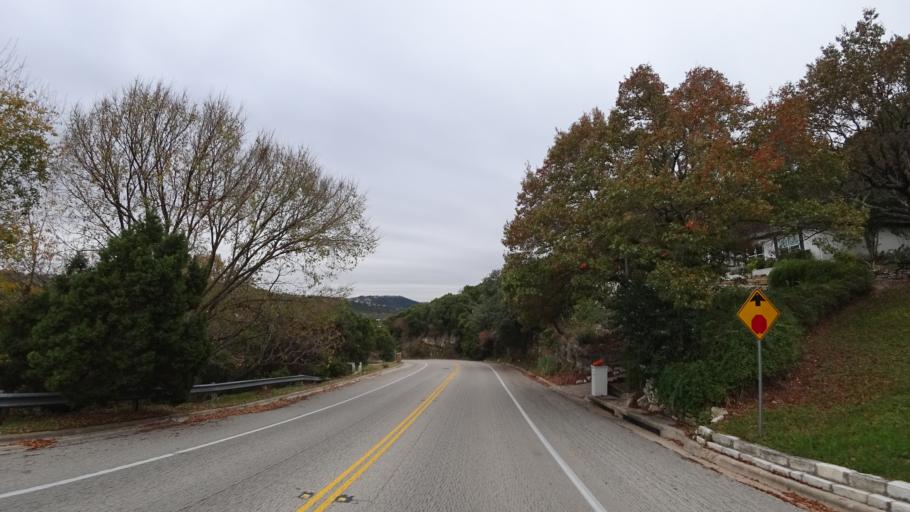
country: US
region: Texas
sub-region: Williamson County
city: Jollyville
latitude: 30.3769
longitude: -97.7909
